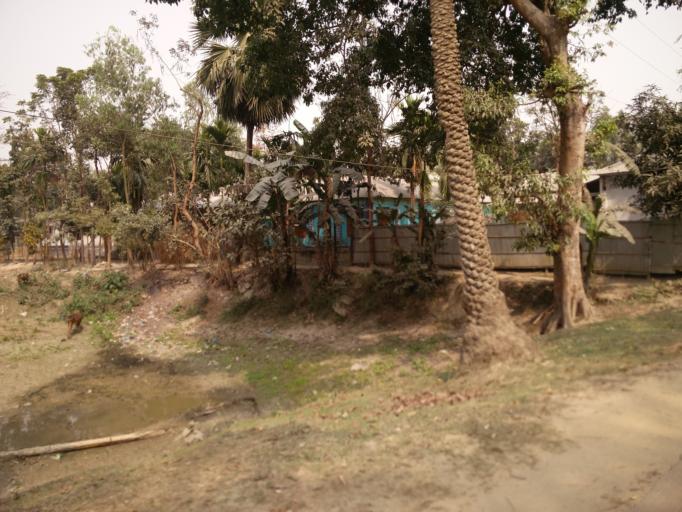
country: BD
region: Rangpur Division
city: Nageswari
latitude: 25.8860
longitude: 89.7035
